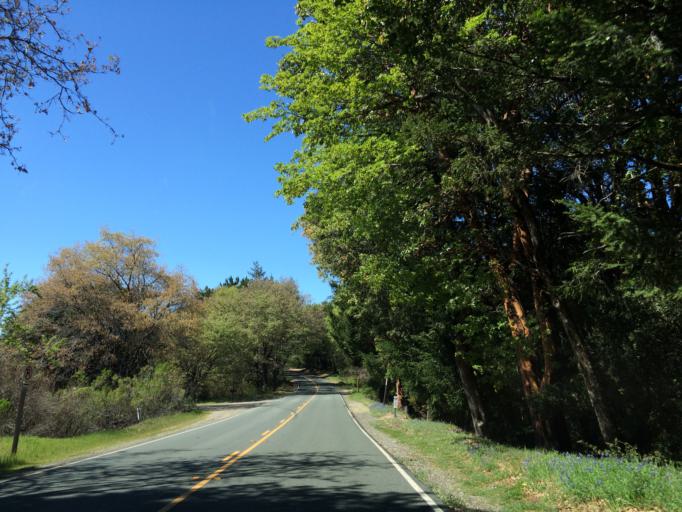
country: US
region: California
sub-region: Santa Clara County
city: Saratoga
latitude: 37.2324
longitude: -122.0981
